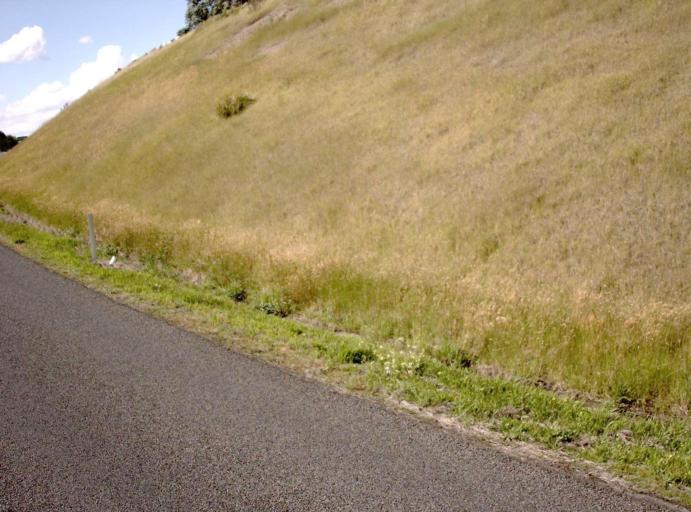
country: AU
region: Victoria
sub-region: Latrobe
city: Moe
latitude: -38.2124
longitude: 146.3200
